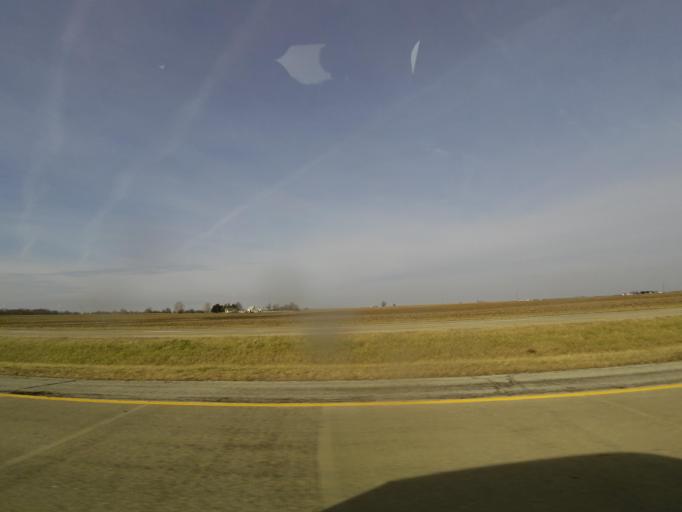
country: US
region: Illinois
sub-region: De Witt County
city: Clinton
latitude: 40.1663
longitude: -88.9778
